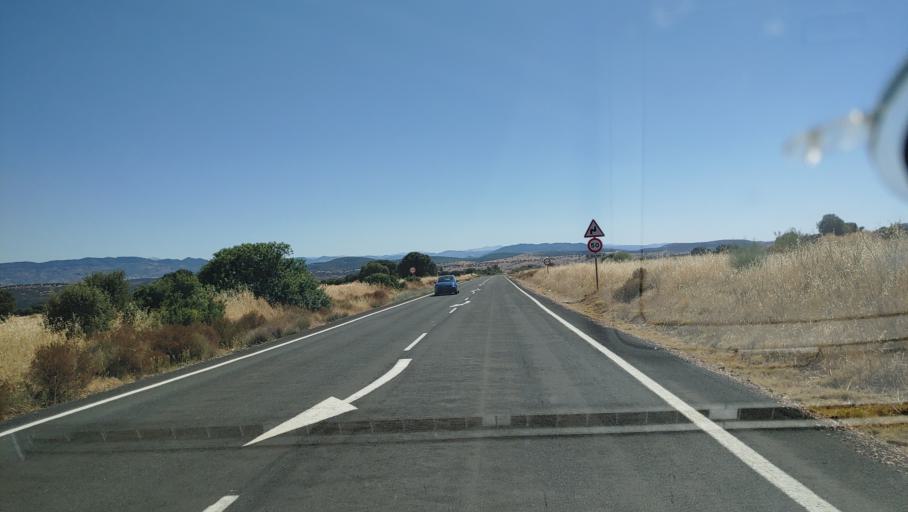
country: ES
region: Castille-La Mancha
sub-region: Provincia de Ciudad Real
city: Albaladejo
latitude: 38.5346
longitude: -2.7862
